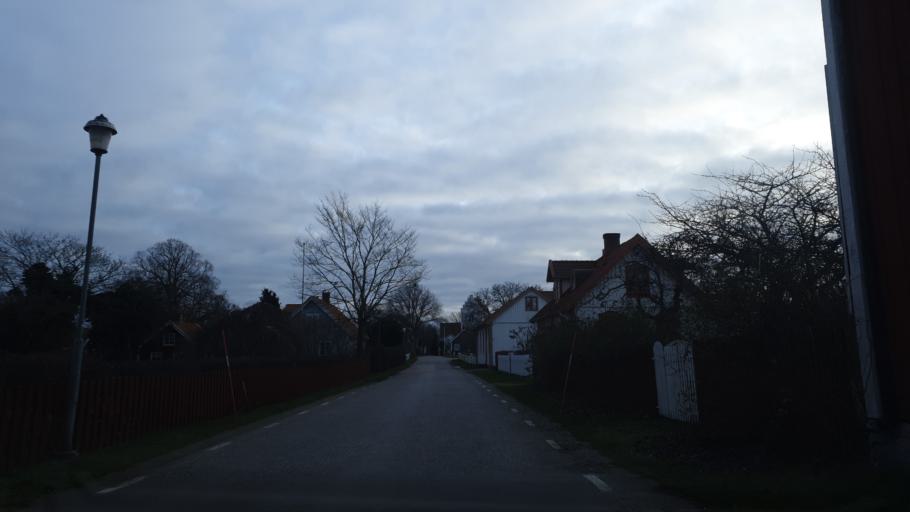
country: SE
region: Kalmar
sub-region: Torsas Kommun
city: Torsas
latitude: 56.2591
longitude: 16.0412
